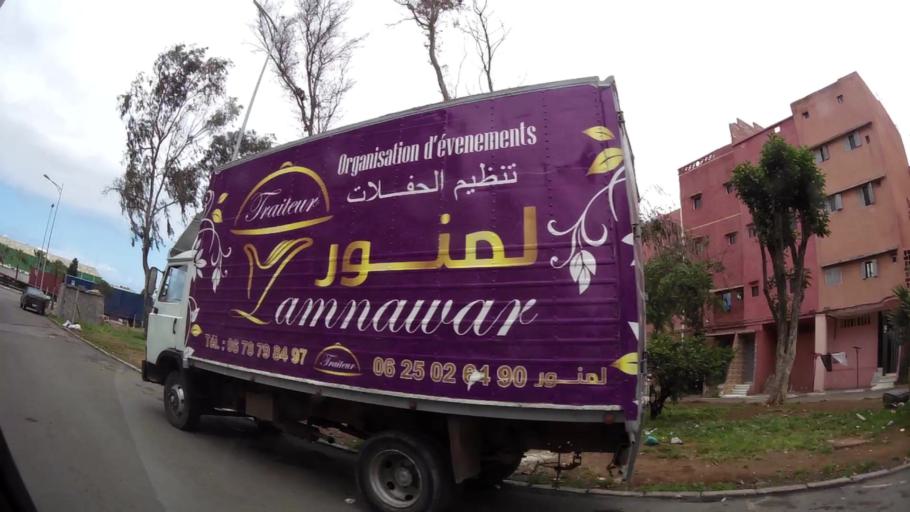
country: MA
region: Grand Casablanca
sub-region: Mediouna
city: Tit Mellil
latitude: 33.6136
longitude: -7.5081
